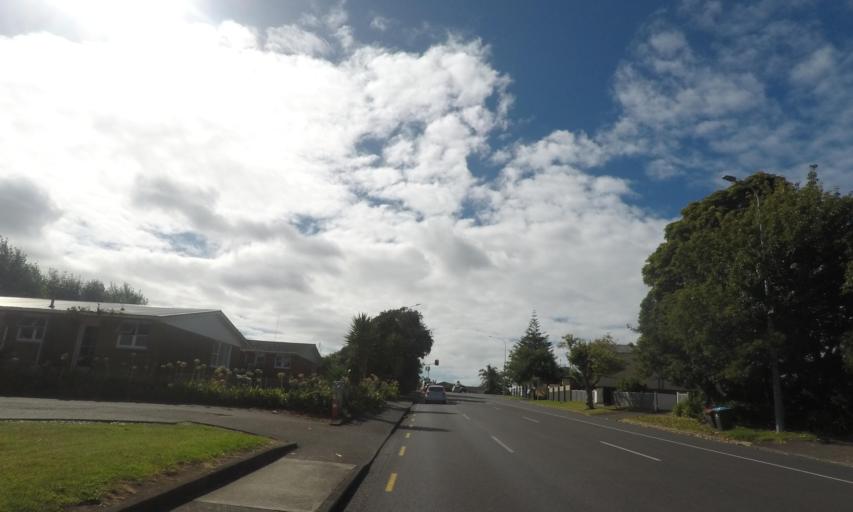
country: NZ
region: Auckland
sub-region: Auckland
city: Tamaki
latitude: -36.9104
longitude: 174.8451
